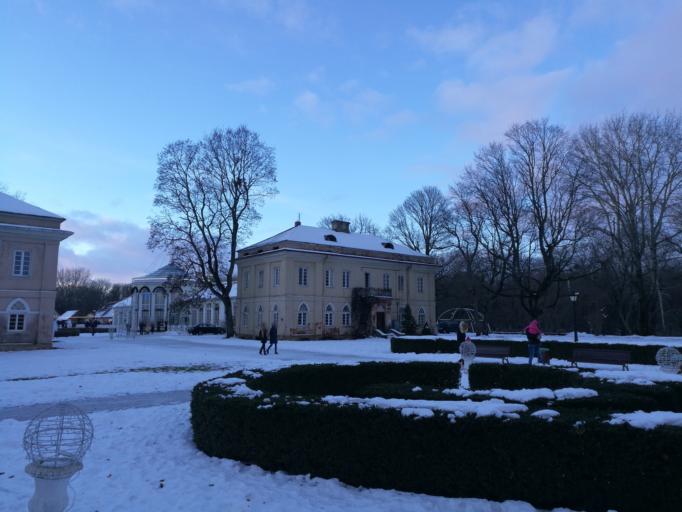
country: LT
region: Kauno apskritis
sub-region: Kauno rajonas
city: Akademija (Kaunas)
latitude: 54.9432
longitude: 23.7842
